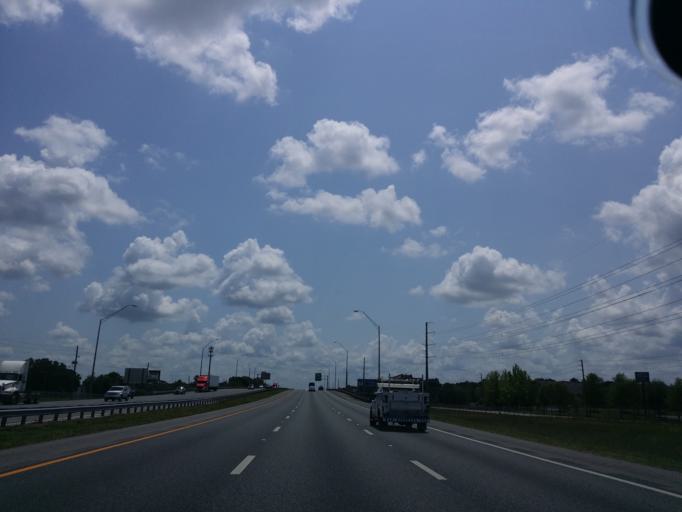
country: US
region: Florida
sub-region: Marion County
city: Ocala
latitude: 29.1722
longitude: -82.1848
